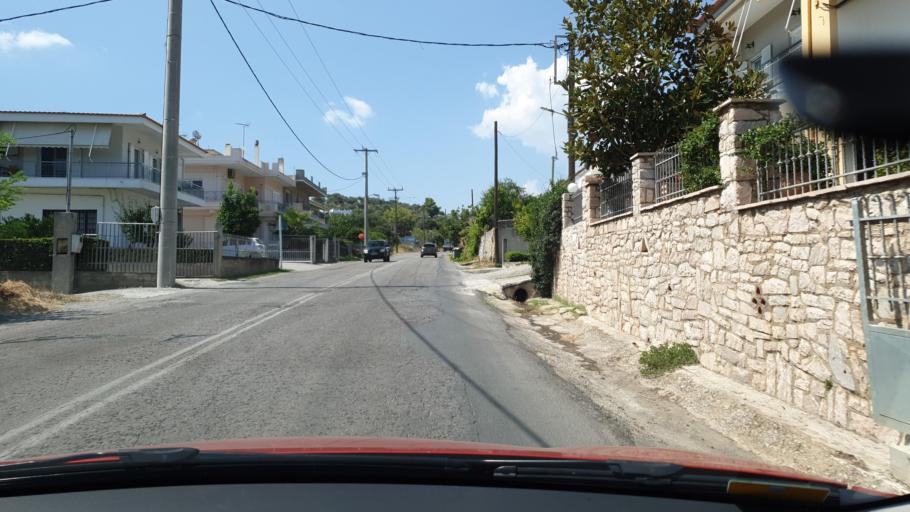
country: GR
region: Central Greece
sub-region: Nomos Evvoias
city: Aliveri
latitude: 38.3916
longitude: 24.0917
